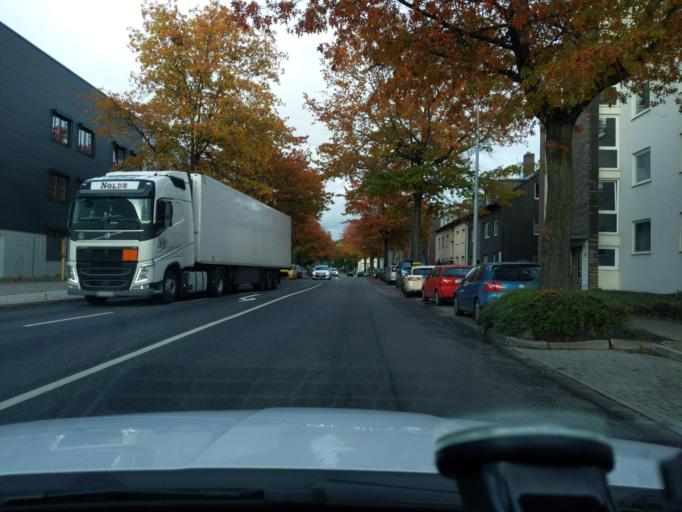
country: DE
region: North Rhine-Westphalia
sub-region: Regierungsbezirk Dusseldorf
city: Hilden
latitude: 51.1706
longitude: 6.8787
